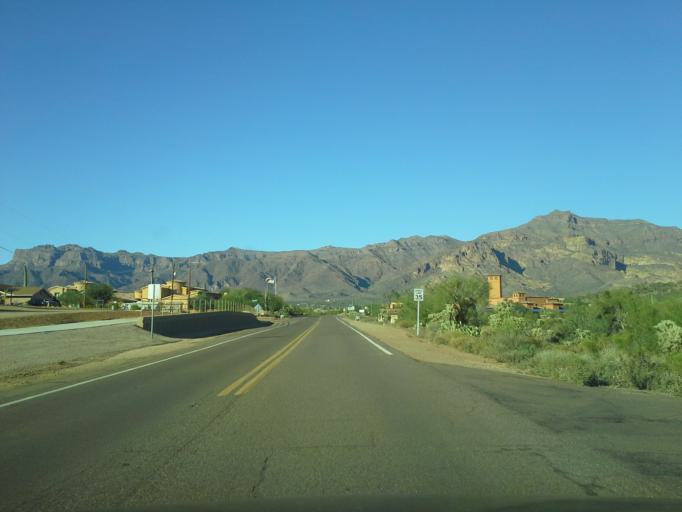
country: US
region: Arizona
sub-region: Pinal County
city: Apache Junction
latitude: 33.3640
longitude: -111.4334
